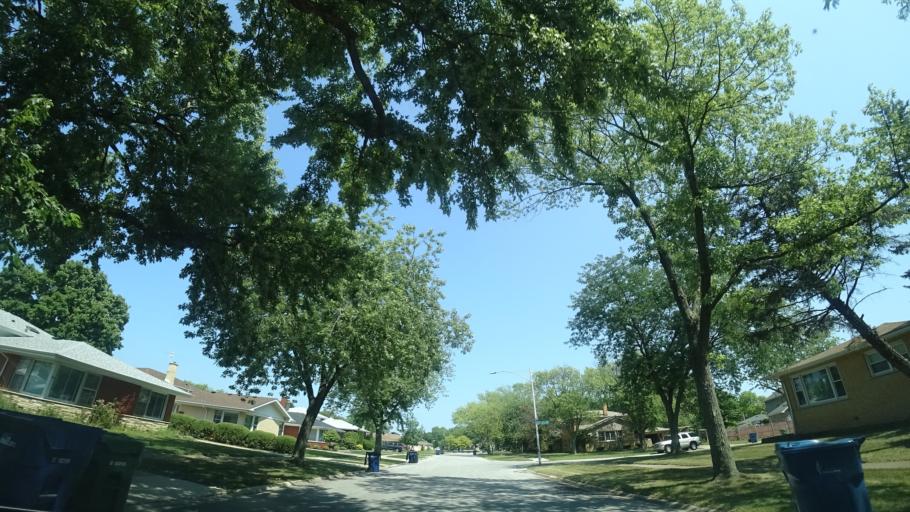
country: US
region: Illinois
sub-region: Cook County
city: Oak Lawn
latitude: 41.7009
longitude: -87.7486
